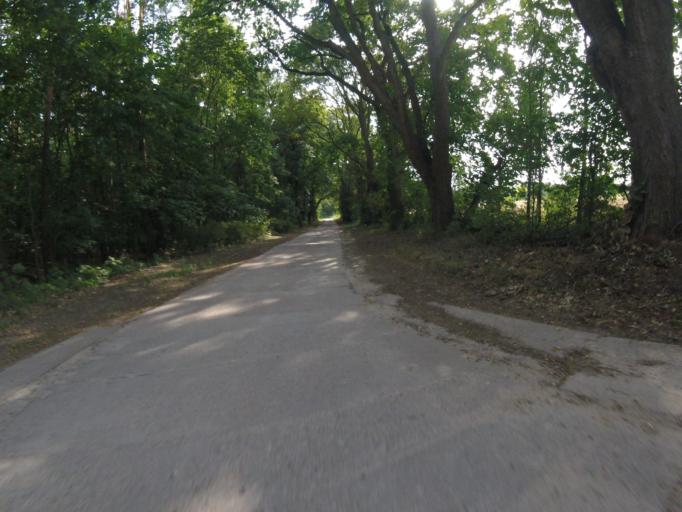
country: DE
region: Brandenburg
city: Munchehofe
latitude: 52.2652
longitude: 13.8053
